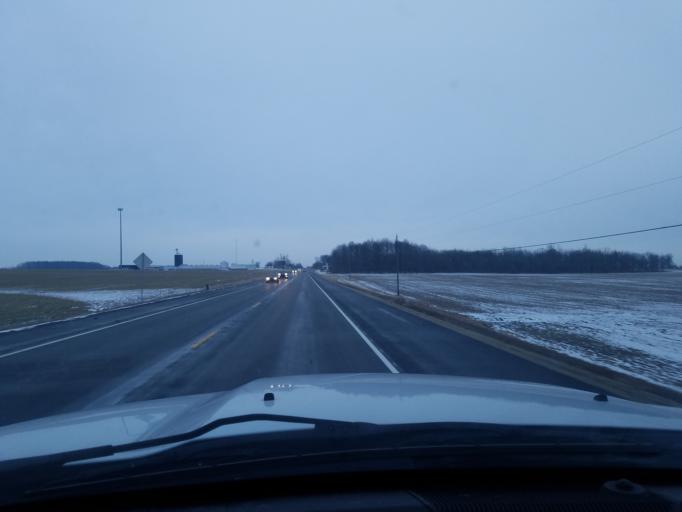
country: US
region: Indiana
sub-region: Randolph County
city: Parker City
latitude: 40.1932
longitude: -85.1935
